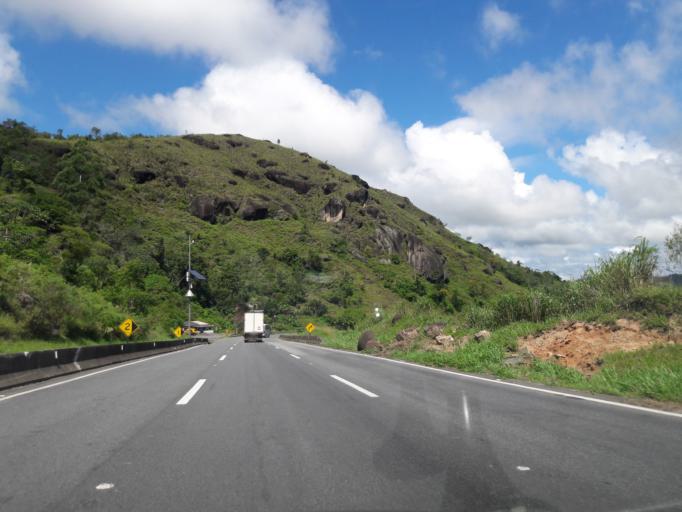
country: BR
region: Sao Paulo
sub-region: Cajati
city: Cajati
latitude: -24.9539
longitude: -48.4510
